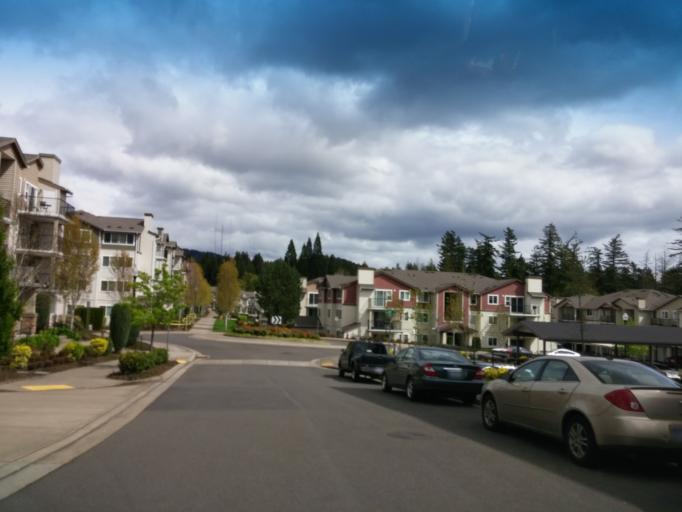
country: US
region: Oregon
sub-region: Washington County
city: Cedar Mill
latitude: 45.5216
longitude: -122.7989
